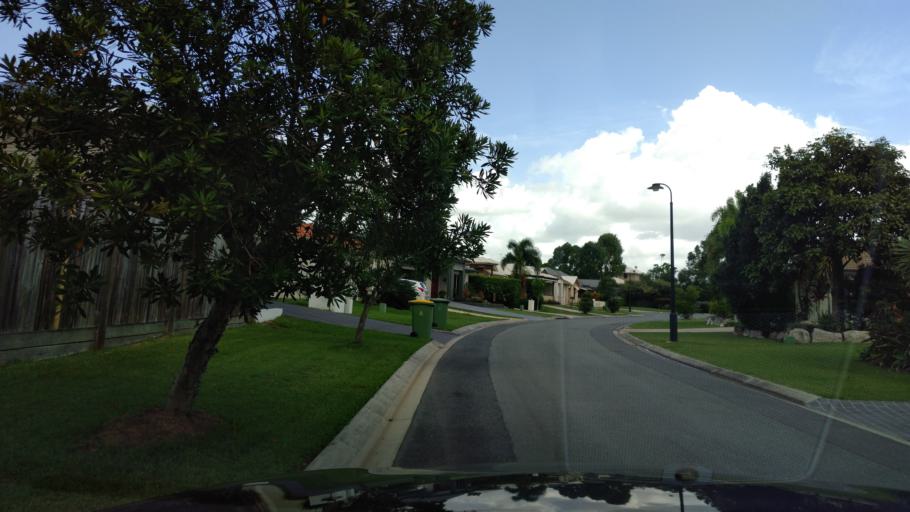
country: AU
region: Queensland
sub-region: Moreton Bay
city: Deception Bay
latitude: -27.2106
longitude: 153.0240
